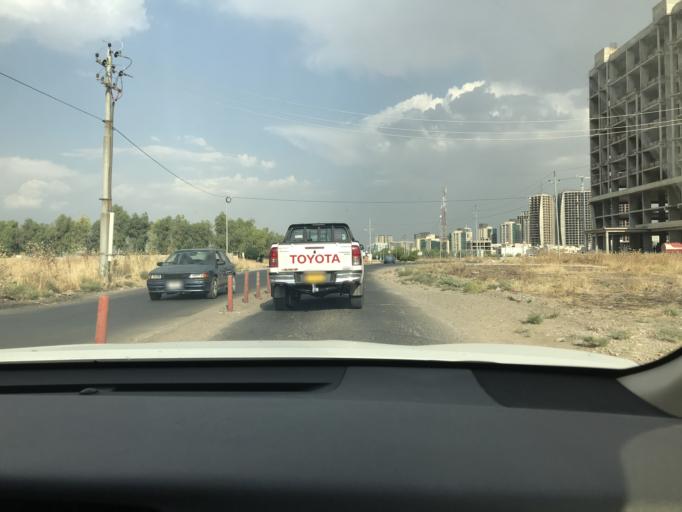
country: IQ
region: Arbil
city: Erbil
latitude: 36.2069
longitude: 43.9599
